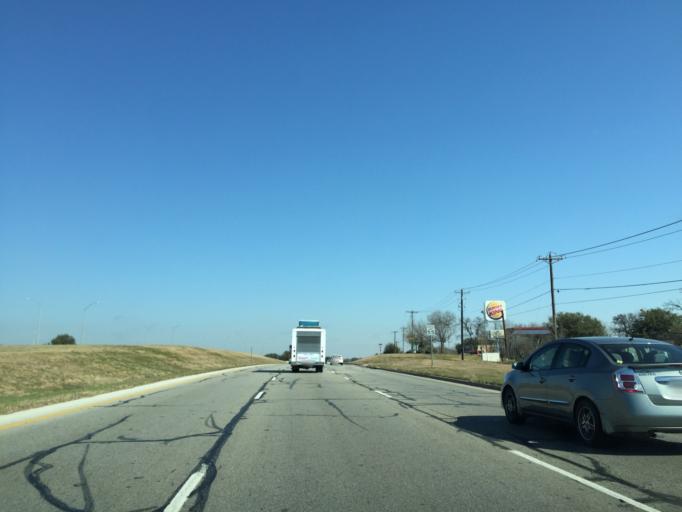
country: US
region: Texas
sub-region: Williamson County
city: Georgetown
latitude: 30.6383
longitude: -97.6890
